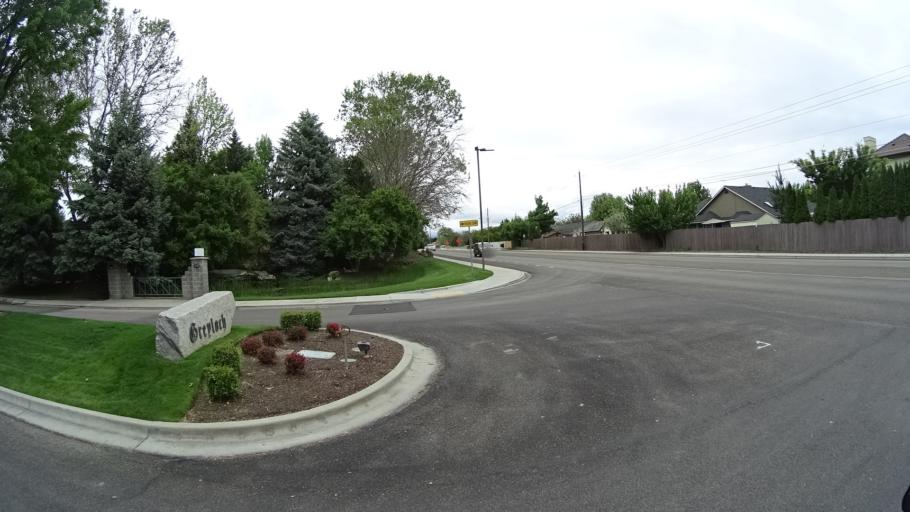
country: US
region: Idaho
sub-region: Ada County
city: Eagle
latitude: 43.6486
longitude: -116.3108
